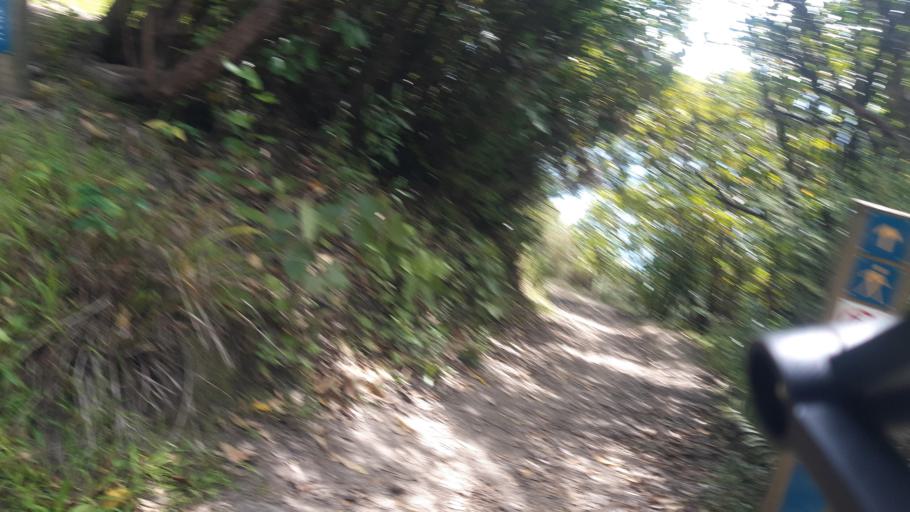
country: NZ
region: Marlborough
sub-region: Marlborough District
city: Picton
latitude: -41.2597
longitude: 174.0355
